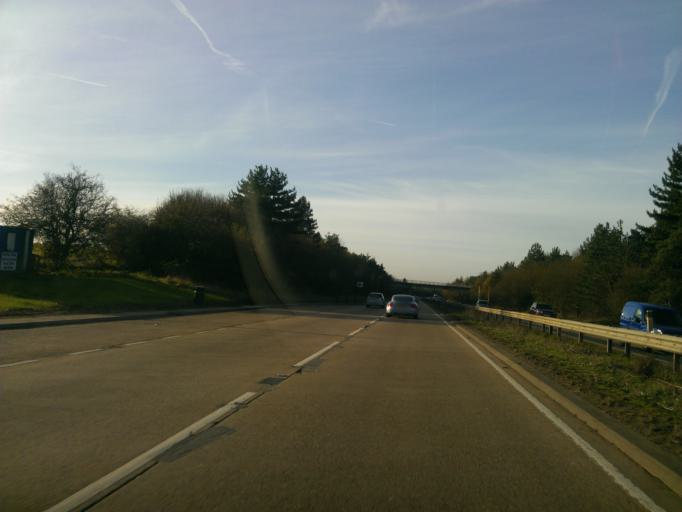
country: GB
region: England
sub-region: Essex
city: Kelvedon
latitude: 51.8331
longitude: 0.7143
